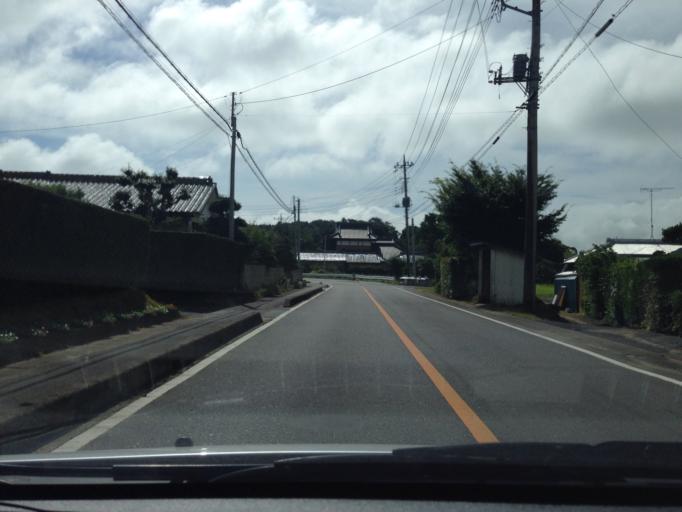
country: JP
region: Ibaraki
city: Inashiki
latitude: 36.0112
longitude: 140.3570
